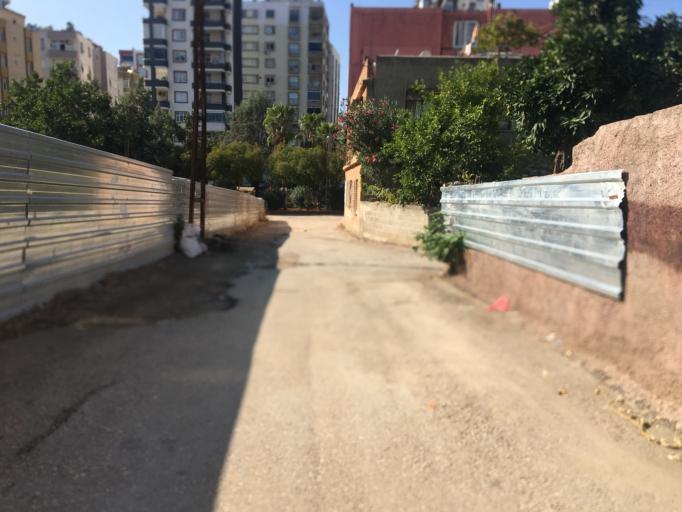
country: TR
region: Adana
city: Seyhan
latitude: 37.0297
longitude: 35.2874
